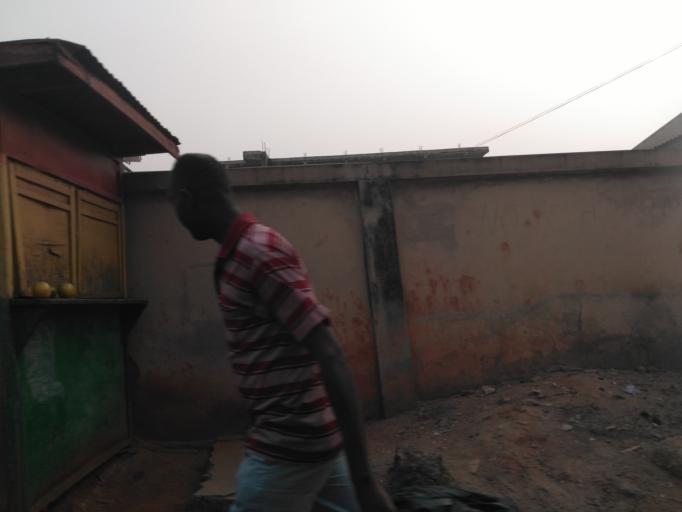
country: GH
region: Ashanti
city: Kumasi
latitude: 6.6884
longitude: -1.6203
